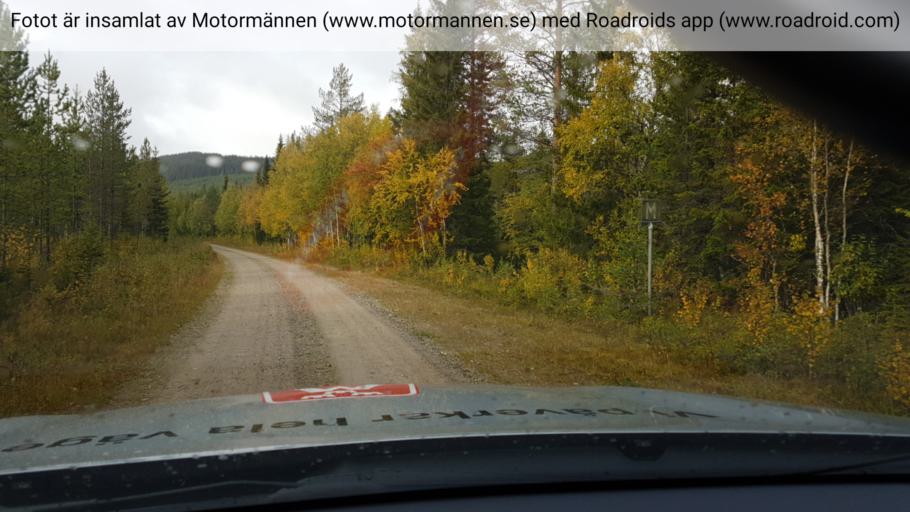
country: SE
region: Jaemtland
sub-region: Harjedalens Kommun
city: Sveg
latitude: 62.2525
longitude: 13.2778
